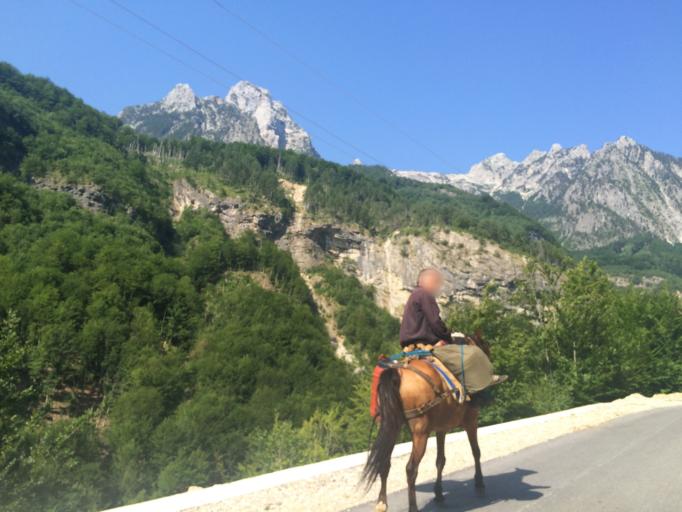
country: AL
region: Kukes
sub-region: Rrethi i Tropojes
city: Valbone
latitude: 42.4399
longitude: 19.9627
